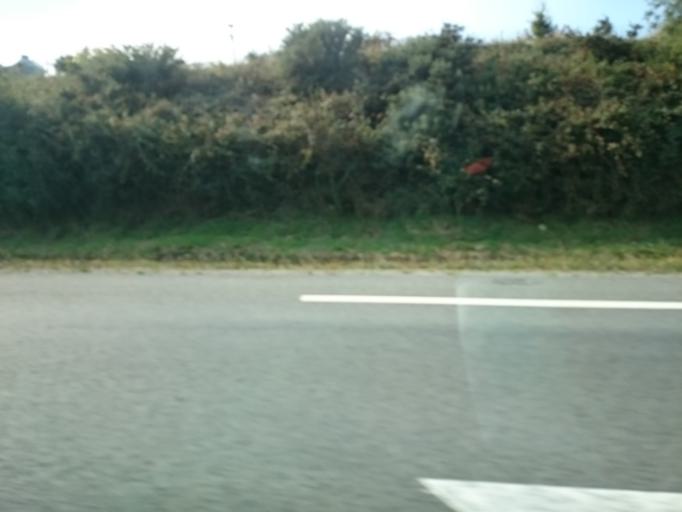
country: FR
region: Brittany
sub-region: Departement d'Ille-et-Vilaine
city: Grand-Fougeray
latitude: 47.7482
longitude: -1.7155
